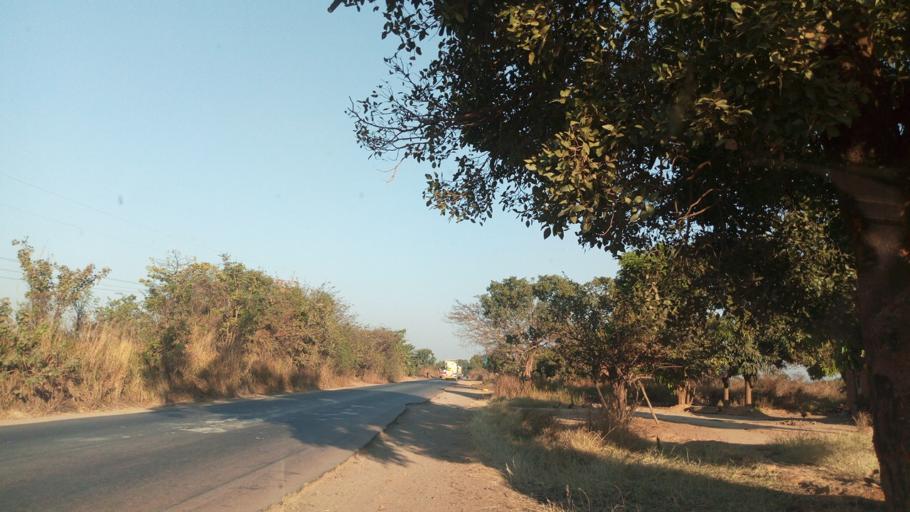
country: CD
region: Katanga
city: Likasi
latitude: -11.1239
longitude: 27.0350
